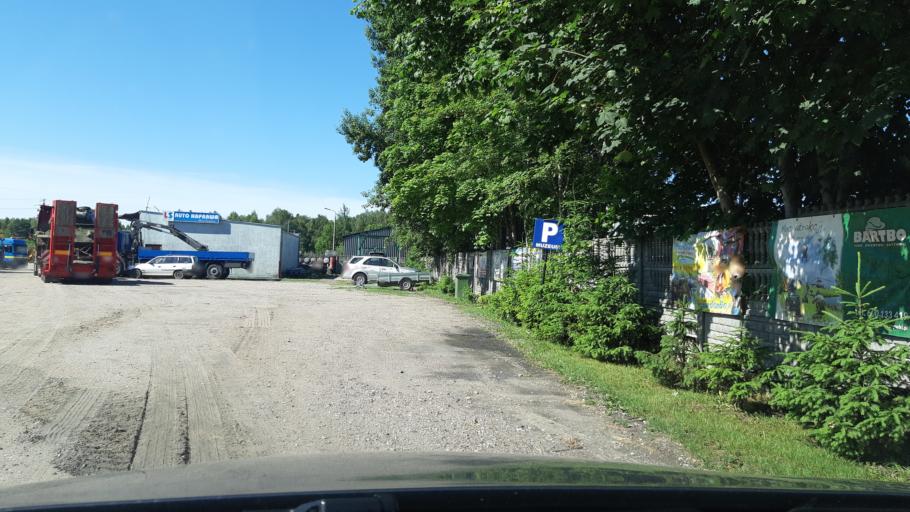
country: PL
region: Warmian-Masurian Voivodeship
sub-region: Powiat mragowski
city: Mragowo
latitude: 53.8506
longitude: 21.2939
